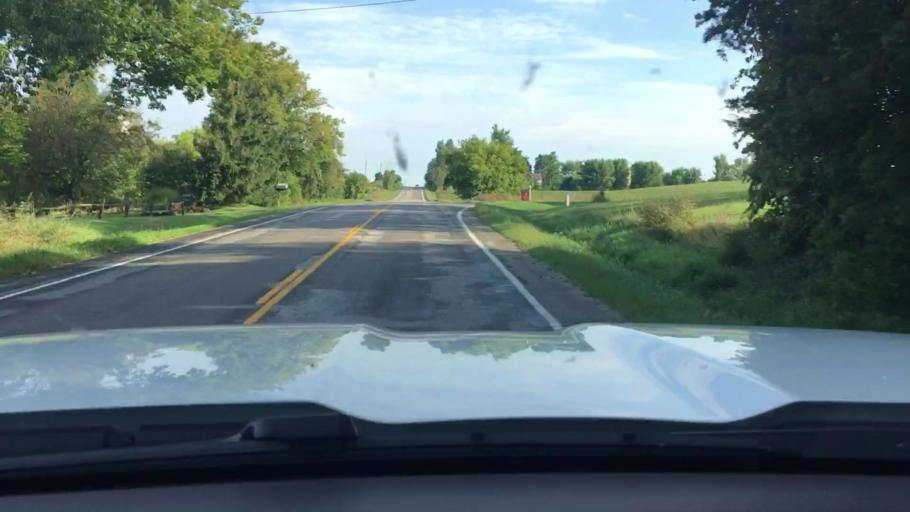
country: US
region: Michigan
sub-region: Kent County
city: Kent City
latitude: 43.2117
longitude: -85.7709
